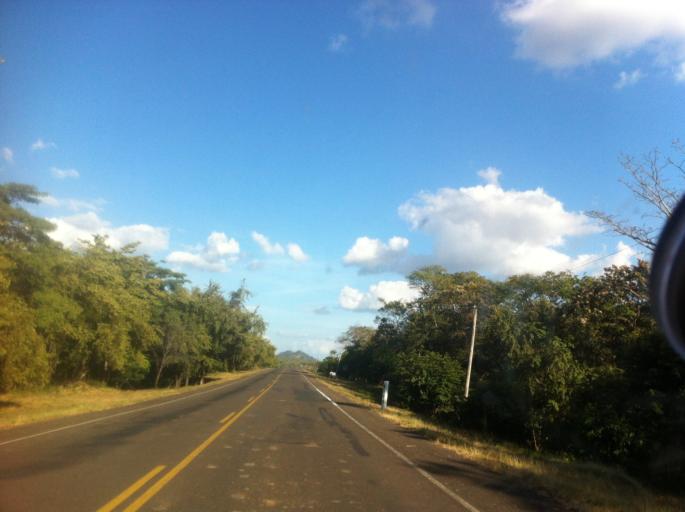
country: NI
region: Chontales
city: Acoyapa
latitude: 11.8705
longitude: -85.0817
